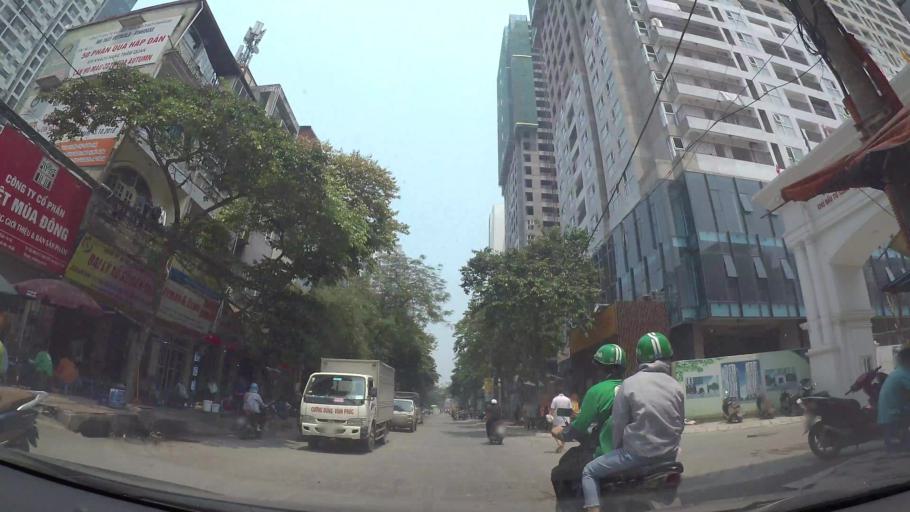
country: VN
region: Ha Noi
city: Thanh Xuan
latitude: 20.9954
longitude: 105.8058
